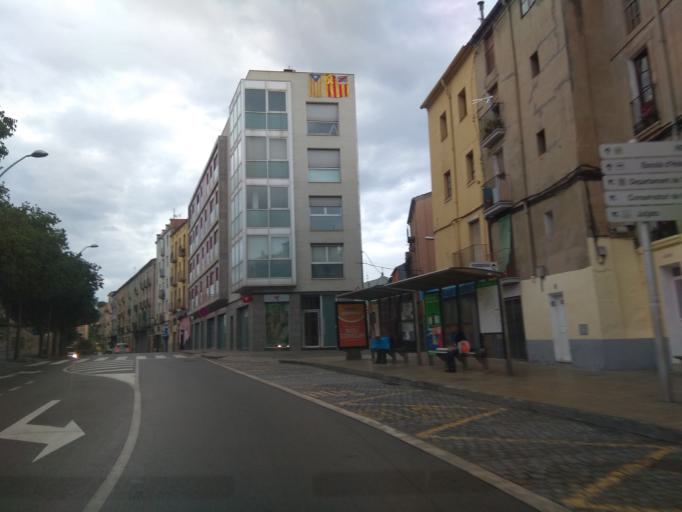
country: ES
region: Catalonia
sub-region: Provincia de Barcelona
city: Manresa
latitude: 41.7241
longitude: 1.8215
